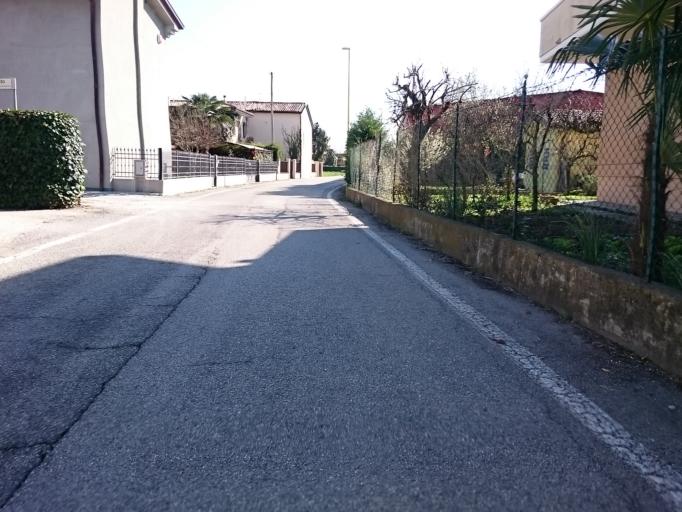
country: IT
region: Veneto
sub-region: Provincia di Padova
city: Ponte San Nicolo
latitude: 45.3818
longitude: 11.9139
